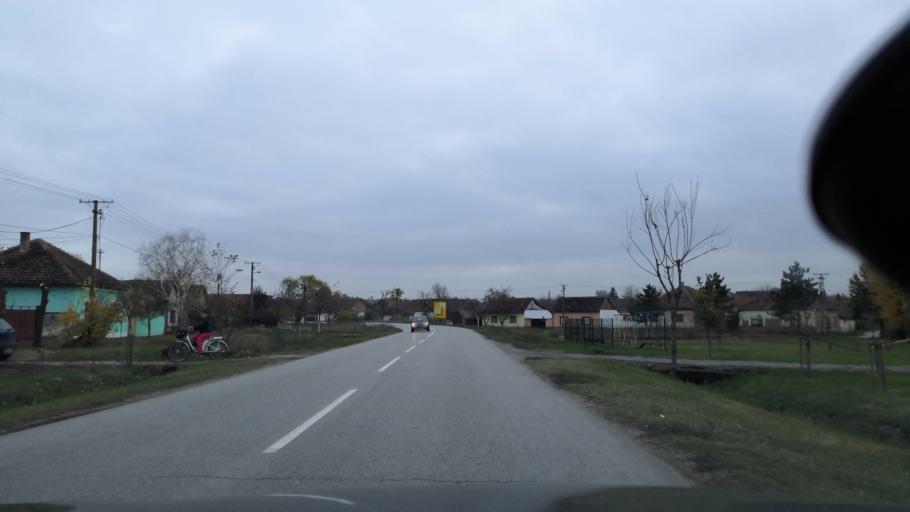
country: RS
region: Autonomna Pokrajina Vojvodina
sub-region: Severnobanatski Okrug
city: Novi Knezevac
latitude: 46.0534
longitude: 20.0997
